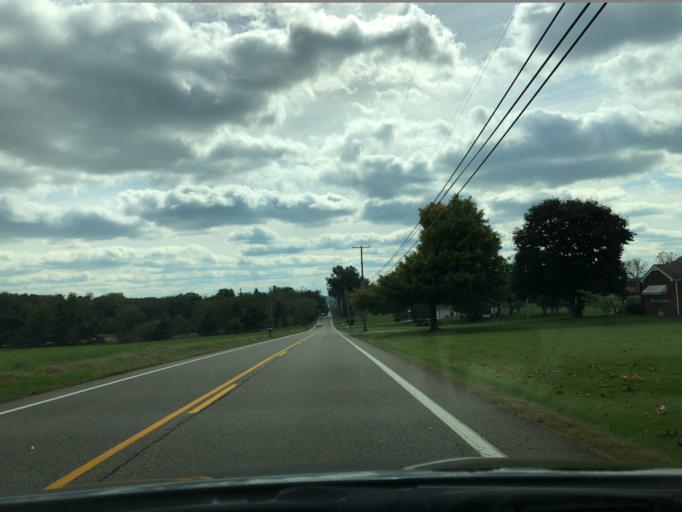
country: US
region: Ohio
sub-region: Stark County
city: Brewster
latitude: 40.7458
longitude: -81.5956
